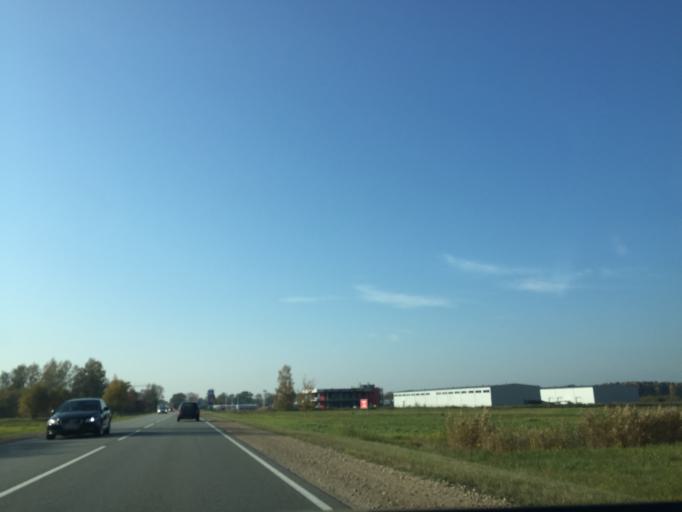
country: LV
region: Babite
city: Pinki
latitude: 56.8819
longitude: 23.9690
